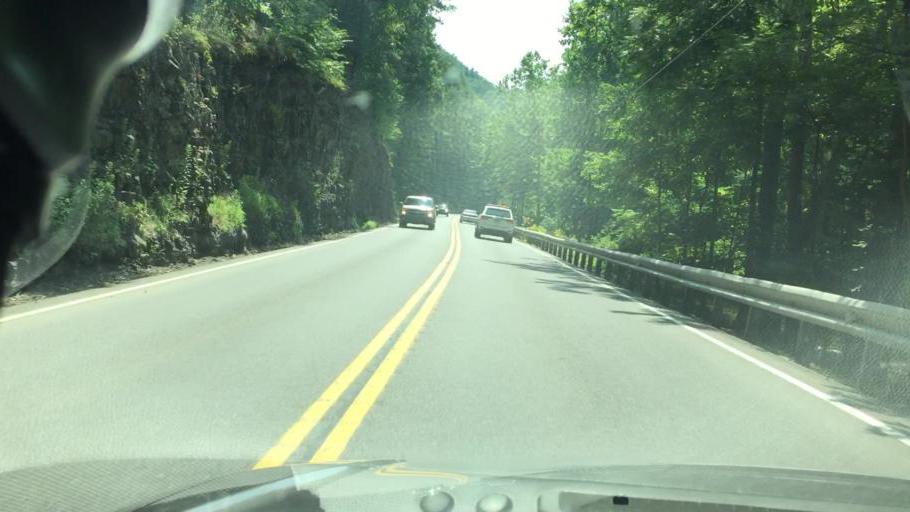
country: US
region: Pennsylvania
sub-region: Northumberland County
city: Elysburg
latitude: 40.8879
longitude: -76.5079
